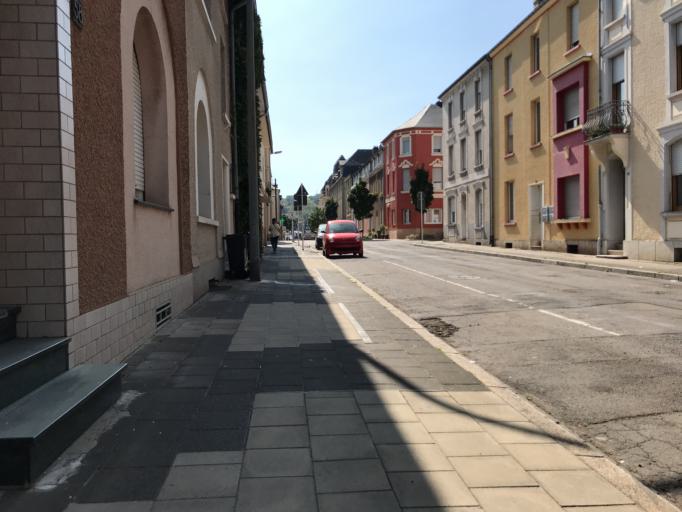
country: LU
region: Luxembourg
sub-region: Canton d'Esch-sur-Alzette
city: Esch-sur-Alzette
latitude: 49.4981
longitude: 5.9777
